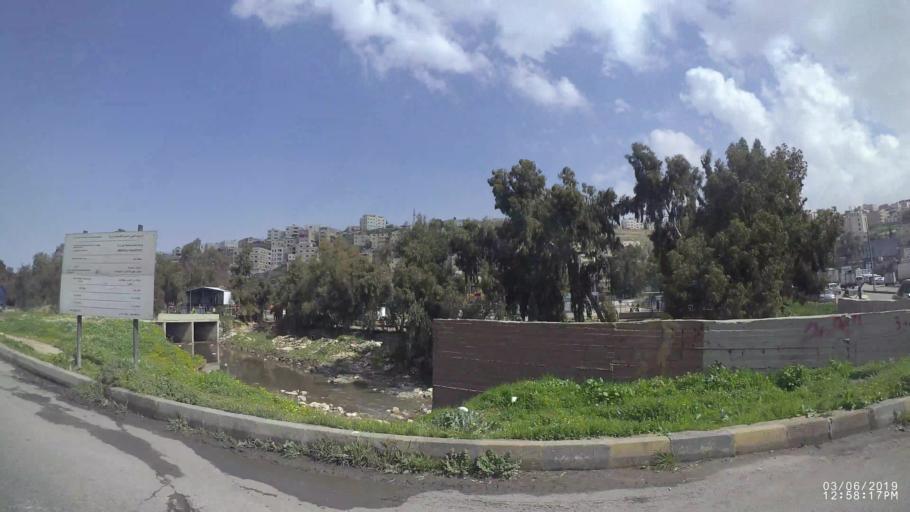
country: JO
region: Amman
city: Amman
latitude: 31.9823
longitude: 35.9754
